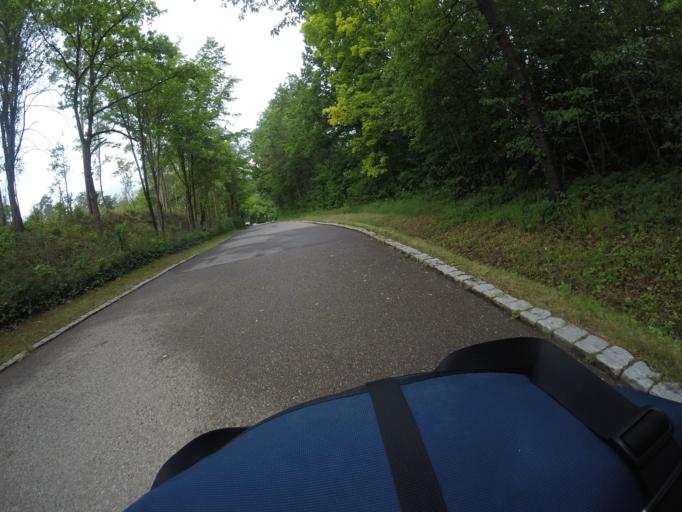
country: DE
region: Baden-Wuerttemberg
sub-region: Regierungsbezirk Stuttgart
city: Gerlingen
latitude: 48.7850
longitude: 9.0713
